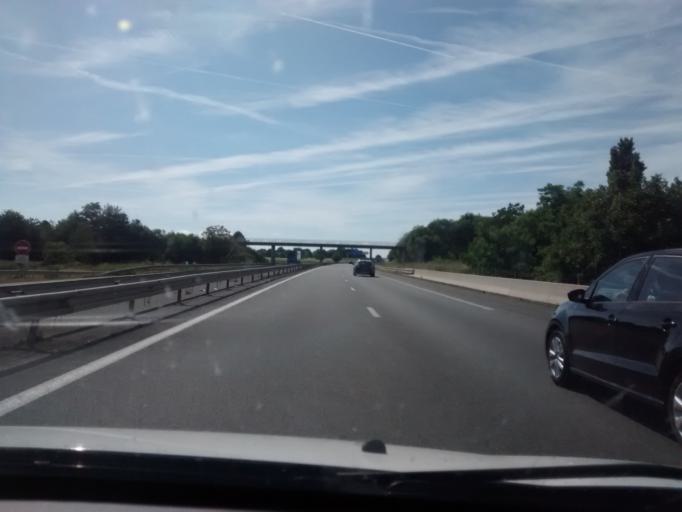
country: FR
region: Pays de la Loire
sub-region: Departement de la Sarthe
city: Brulon
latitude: 48.0036
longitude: -0.2035
